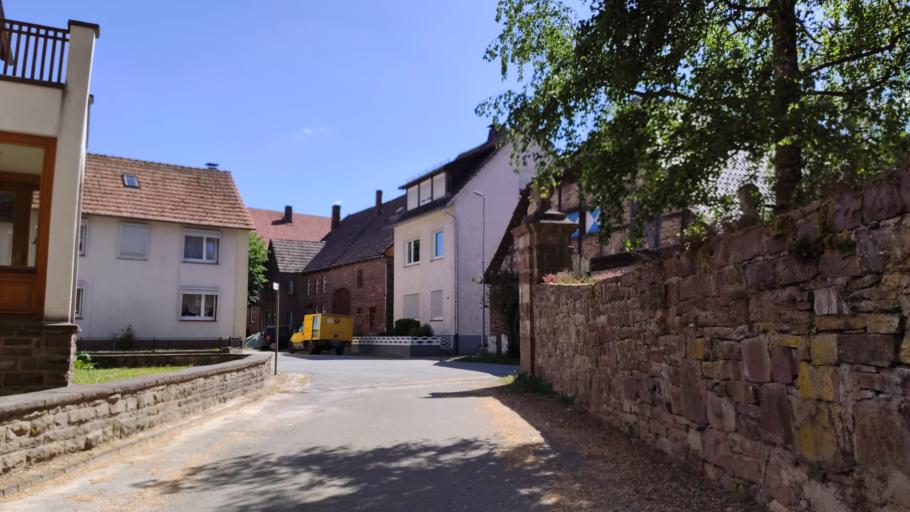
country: DE
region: North Rhine-Westphalia
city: Beverungen
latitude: 51.7127
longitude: 9.3408
